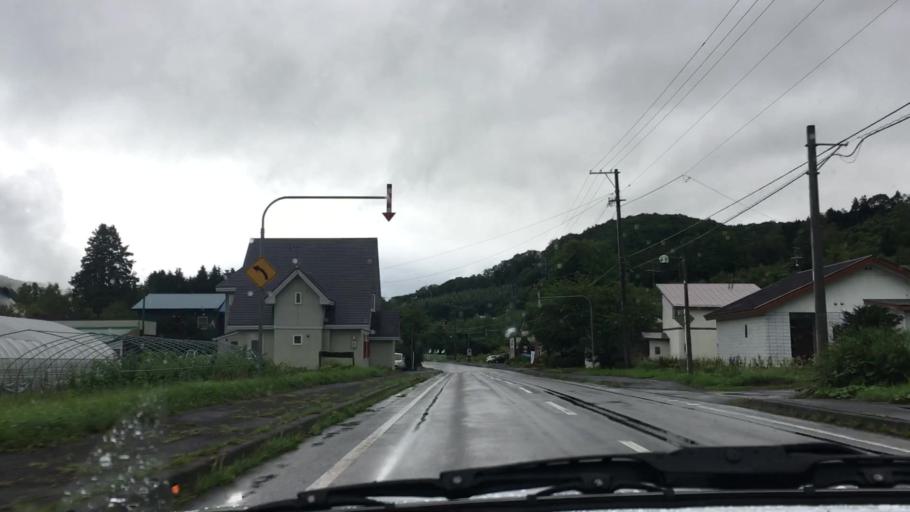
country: JP
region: Hokkaido
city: Niseko Town
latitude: 42.6464
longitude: 140.7336
